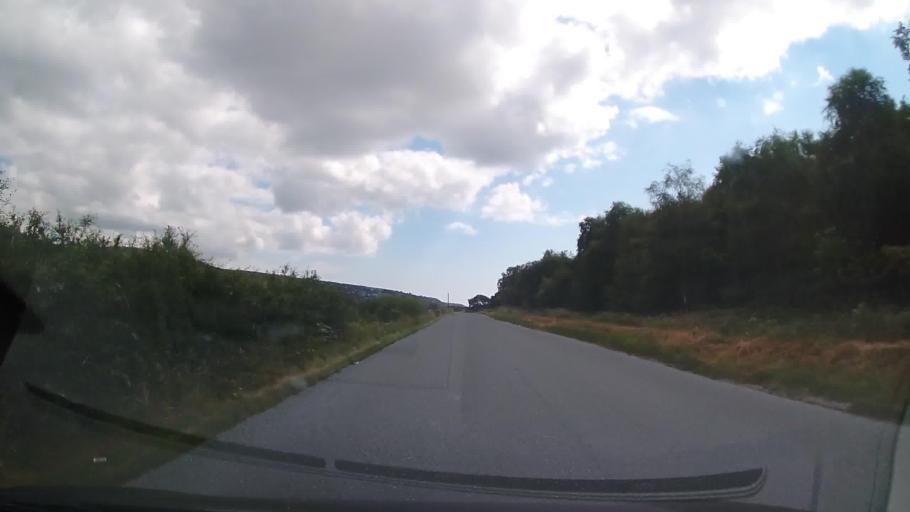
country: GB
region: Wales
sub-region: Gwynedd
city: Llanfair
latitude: 52.8794
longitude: -4.1030
